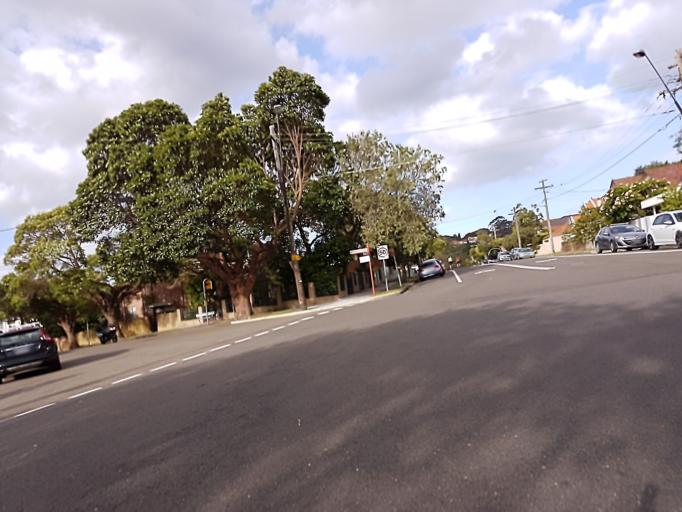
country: AU
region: New South Wales
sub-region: North Sydney
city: Cremorne
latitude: -33.8259
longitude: 151.2246
